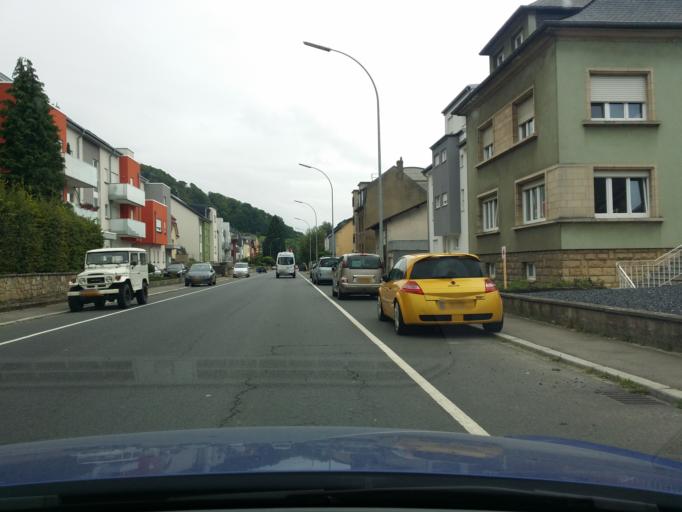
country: LU
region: Luxembourg
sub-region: Canton de Mersch
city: Lintgen
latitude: 49.7175
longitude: 6.1264
